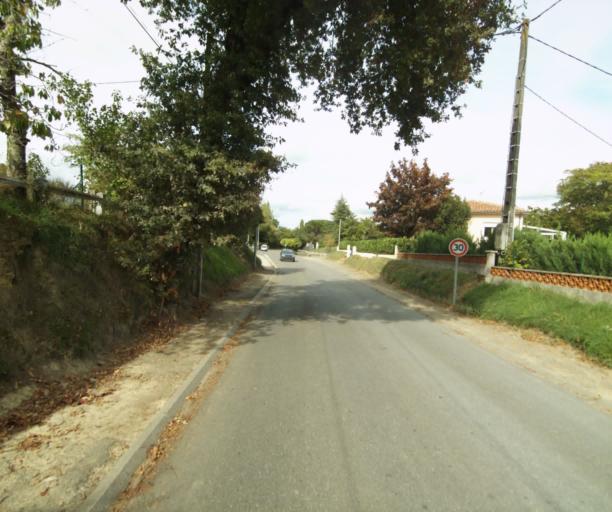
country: FR
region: Midi-Pyrenees
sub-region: Departement du Gers
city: Eauze
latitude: 43.8555
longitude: 0.1027
